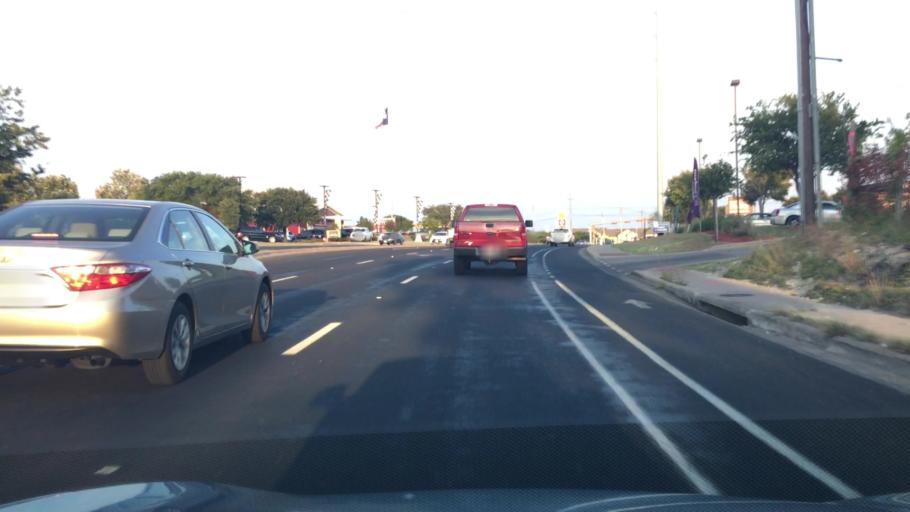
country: US
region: Texas
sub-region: Travis County
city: Onion Creek
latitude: 30.1737
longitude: -97.8016
